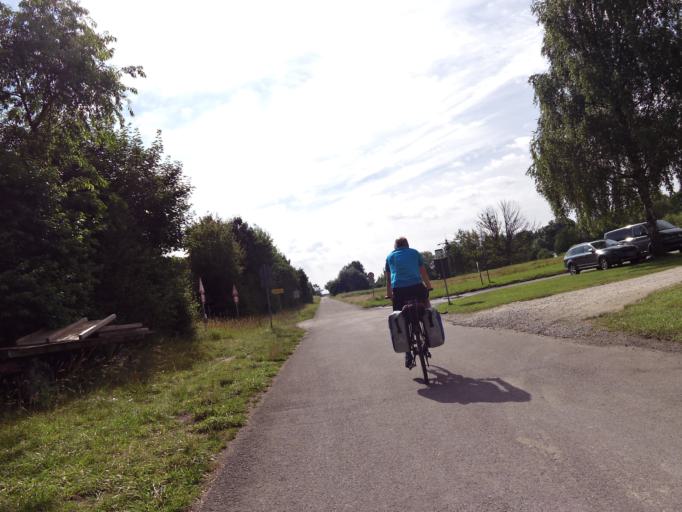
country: DE
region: Baden-Wuerttemberg
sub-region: Freiburg Region
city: Allensbach
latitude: 47.7305
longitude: 9.0255
